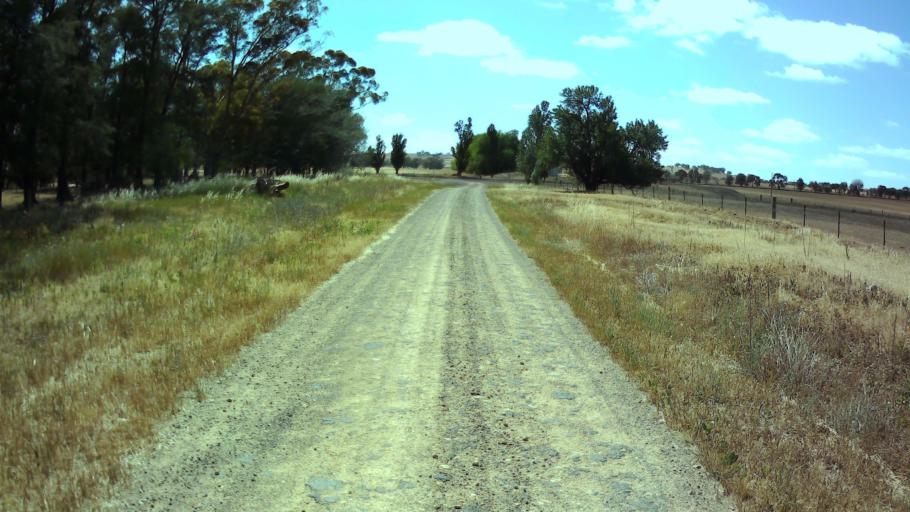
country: AU
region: New South Wales
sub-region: Weddin
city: Grenfell
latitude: -33.9574
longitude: 148.4350
